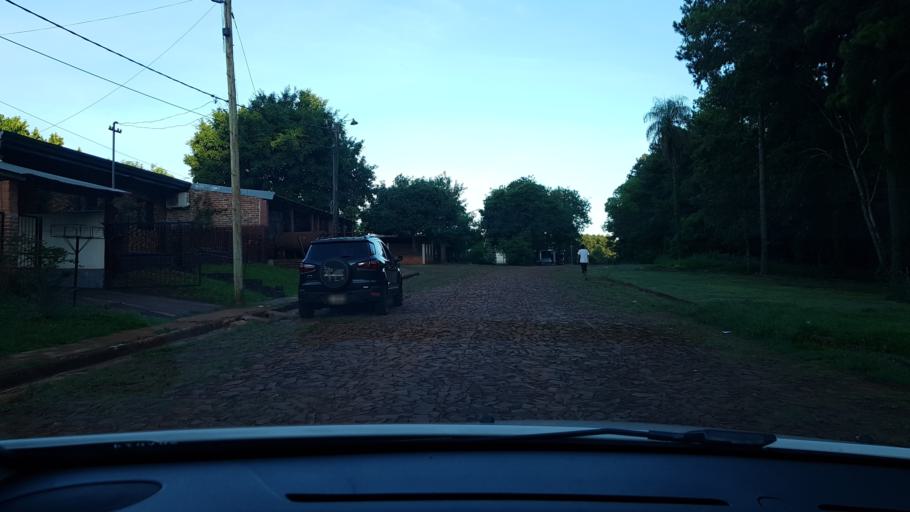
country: AR
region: Misiones
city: Puerto Libertad
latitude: -25.9251
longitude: -54.5815
